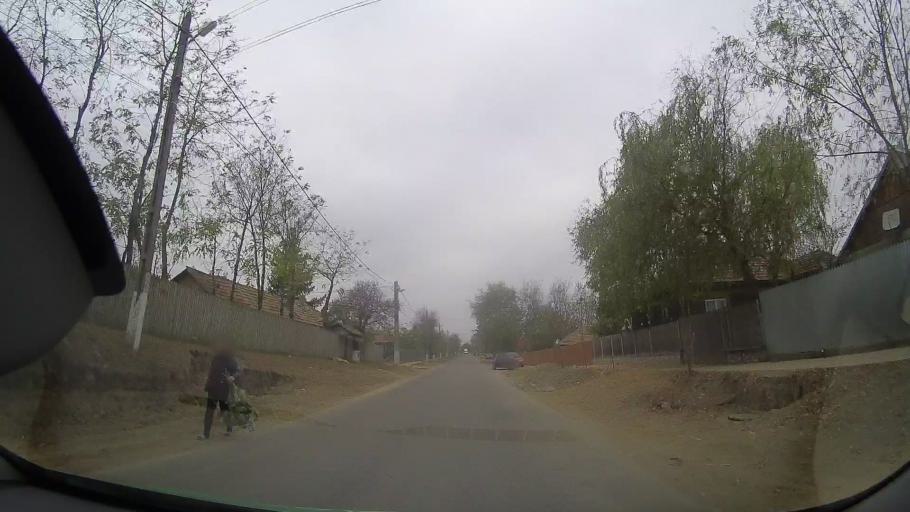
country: RO
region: Buzau
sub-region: Comuna Luciu
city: Luciu
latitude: 44.9685
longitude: 27.0909
